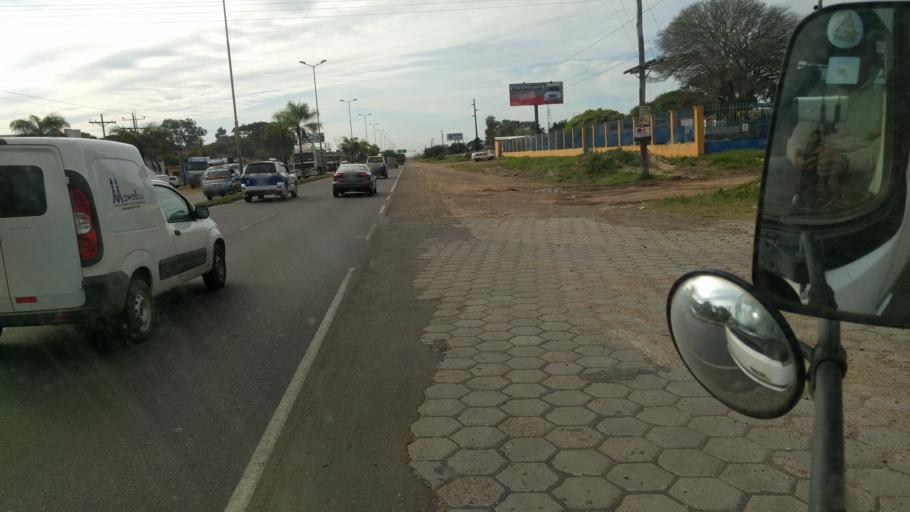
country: BO
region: Santa Cruz
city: Santa Cruz de la Sierra
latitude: -17.6811
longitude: -63.1588
